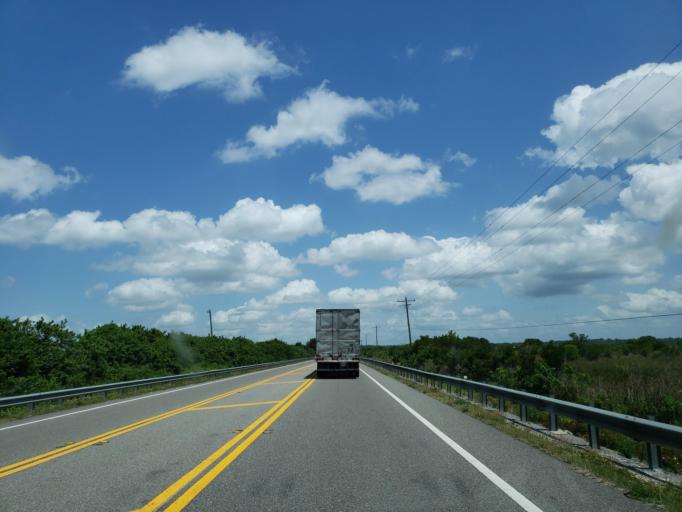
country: US
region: Florida
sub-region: Polk County
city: Babson Park
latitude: 27.8055
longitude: -81.2499
